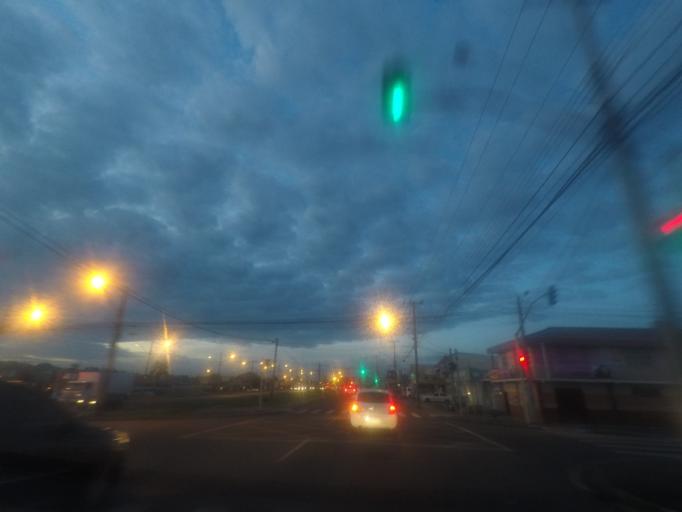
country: BR
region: Parana
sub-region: Pinhais
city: Pinhais
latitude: -25.4028
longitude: -49.1895
